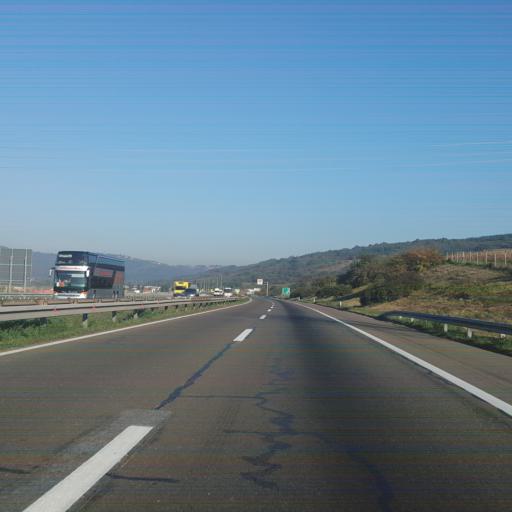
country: RS
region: Central Serbia
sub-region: Belgrade
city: Zvezdara
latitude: 44.7096
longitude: 20.5674
